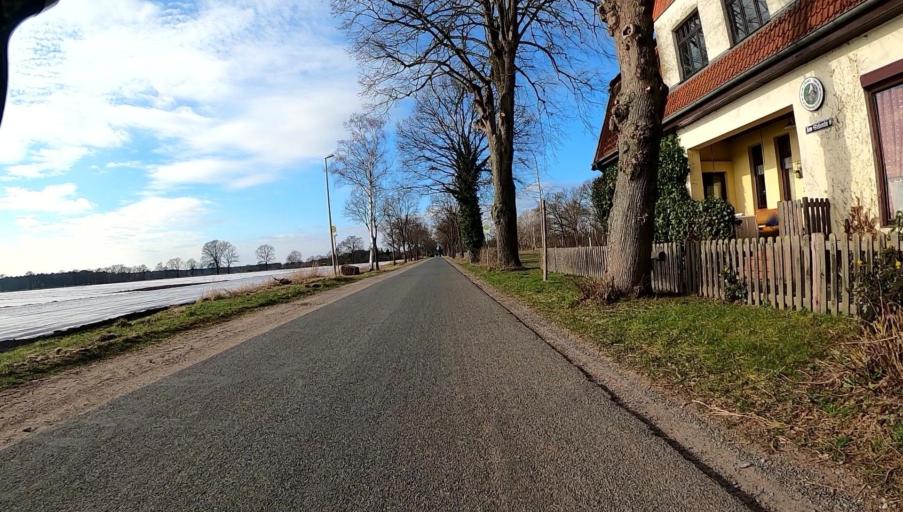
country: DE
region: Lower Saxony
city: Lindwedel
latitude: 52.6109
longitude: 9.6578
